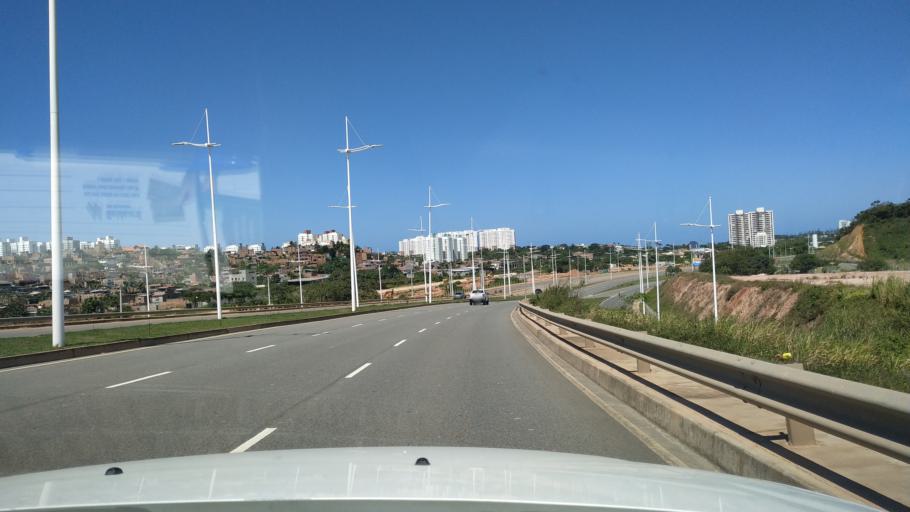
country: BR
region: Bahia
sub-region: Lauro De Freitas
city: Lauro de Freitas
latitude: -12.9280
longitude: -38.3817
